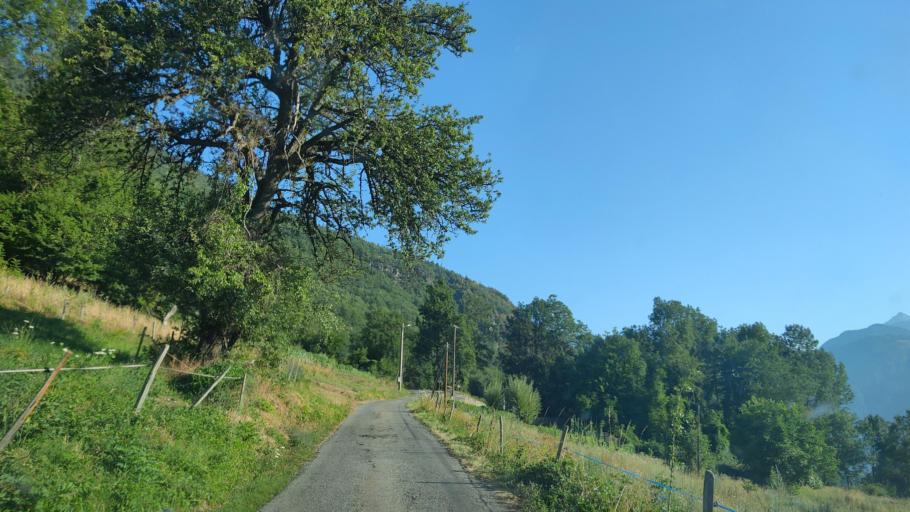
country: FR
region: Rhone-Alpes
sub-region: Departement de la Savoie
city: Saint-Etienne-de-Cuines
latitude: 45.3406
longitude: 6.2829
